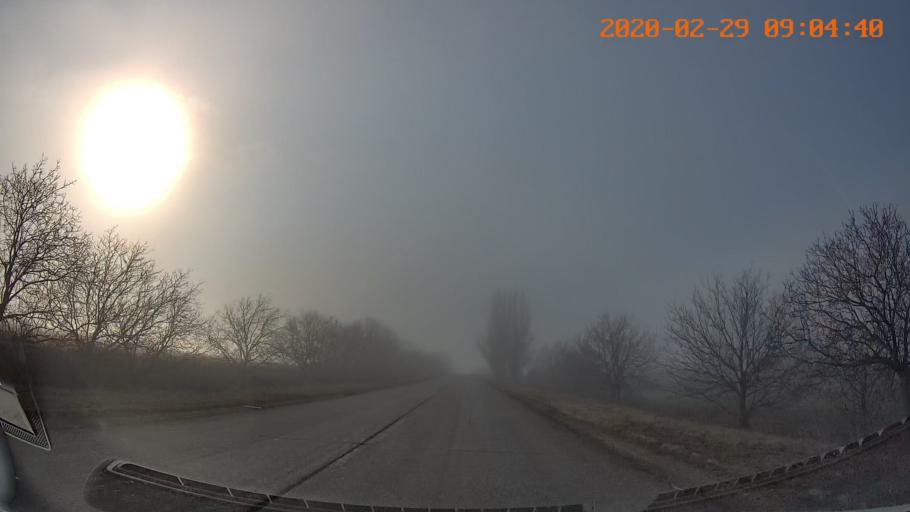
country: MD
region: Telenesti
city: Tiraspolul Nou
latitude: 46.8990
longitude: 29.7371
